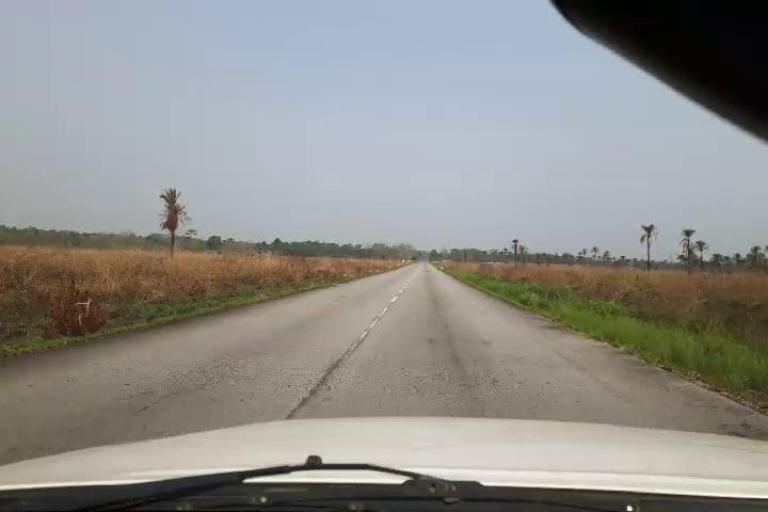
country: SL
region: Southern Province
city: Baiima
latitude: 8.1467
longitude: -11.9043
